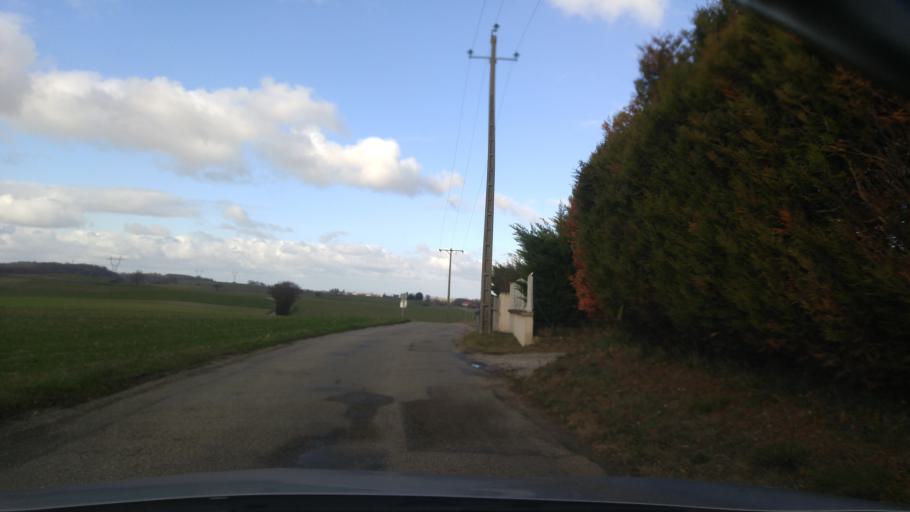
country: FR
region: Rhone-Alpes
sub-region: Departement de l'Isere
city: Roche
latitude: 45.5722
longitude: 5.1837
